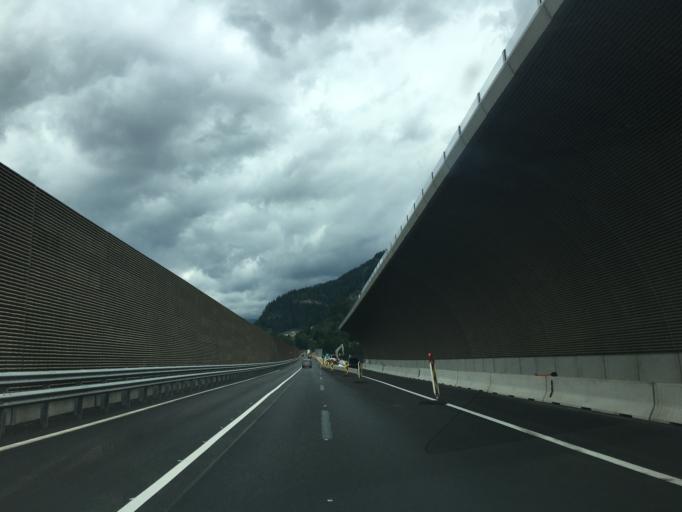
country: AT
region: Salzburg
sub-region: Politischer Bezirk Tamsweg
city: Zederhaus
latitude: 47.1297
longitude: 13.5417
